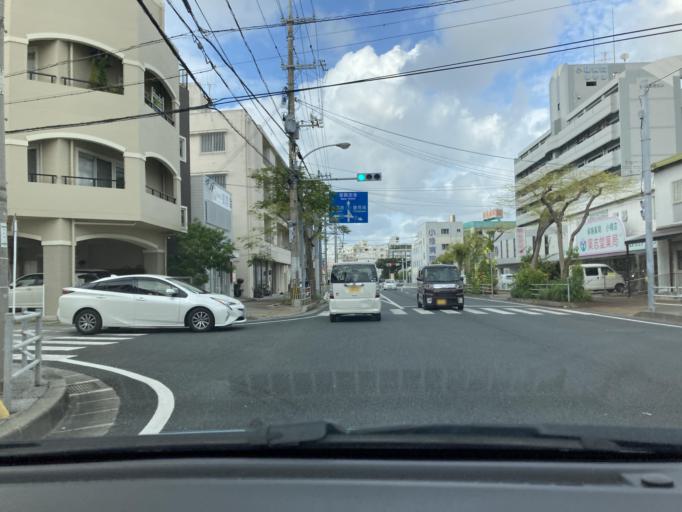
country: JP
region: Okinawa
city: Tomigusuku
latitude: 26.1926
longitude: 127.6756
